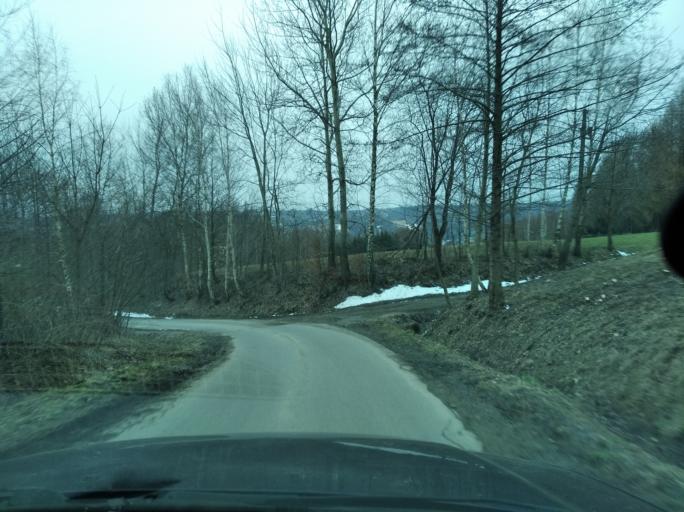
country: PL
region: Subcarpathian Voivodeship
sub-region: Powiat rzeszowski
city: Chmielnik
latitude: 49.9874
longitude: 22.1350
